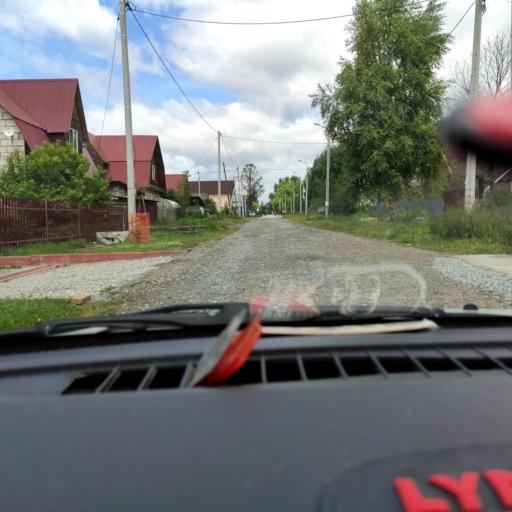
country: RU
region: Perm
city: Perm
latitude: 58.0760
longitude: 56.3580
